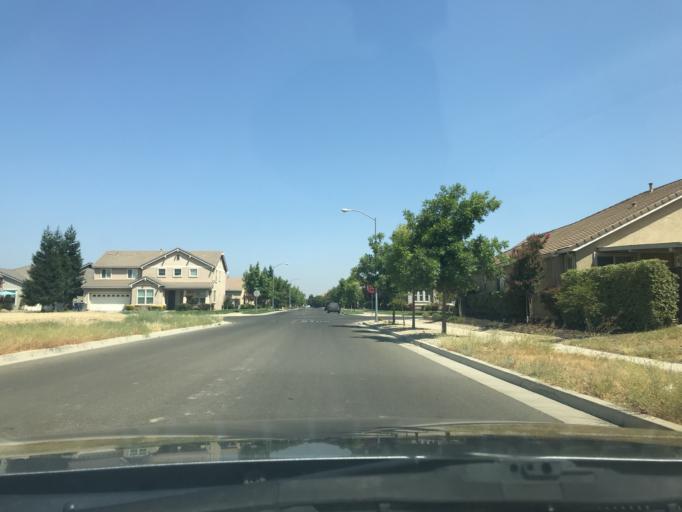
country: US
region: California
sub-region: Merced County
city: Merced
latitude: 37.3501
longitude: -120.4744
